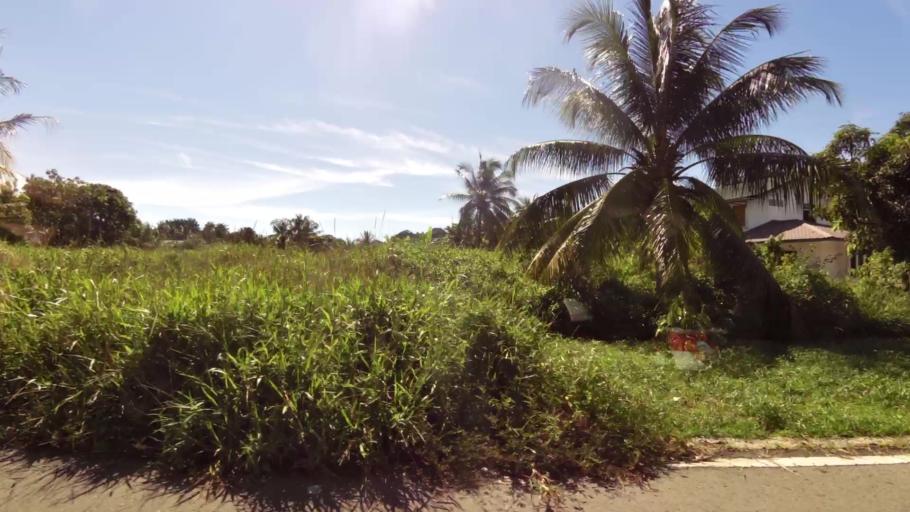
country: BN
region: Brunei and Muara
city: Bandar Seri Begawan
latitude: 5.0030
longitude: 115.0495
